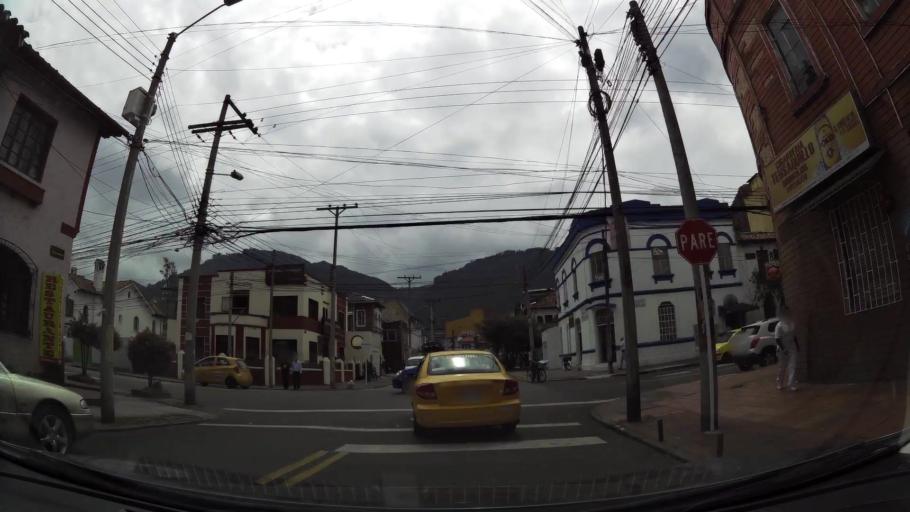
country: CO
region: Bogota D.C.
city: Bogota
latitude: 4.6223
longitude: -74.0706
